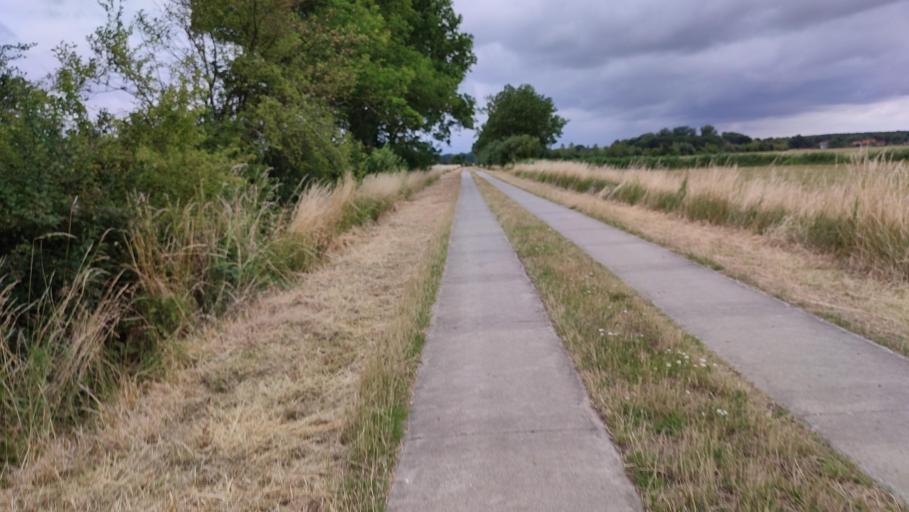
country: DE
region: Lower Saxony
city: Hitzacker
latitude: 53.1715
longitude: 11.1022
